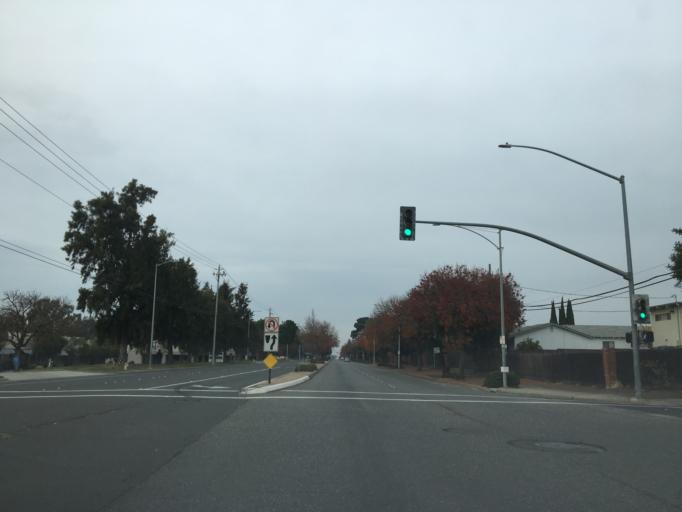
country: US
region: California
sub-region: Santa Clara County
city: Milpitas
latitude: 37.4774
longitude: -121.9223
